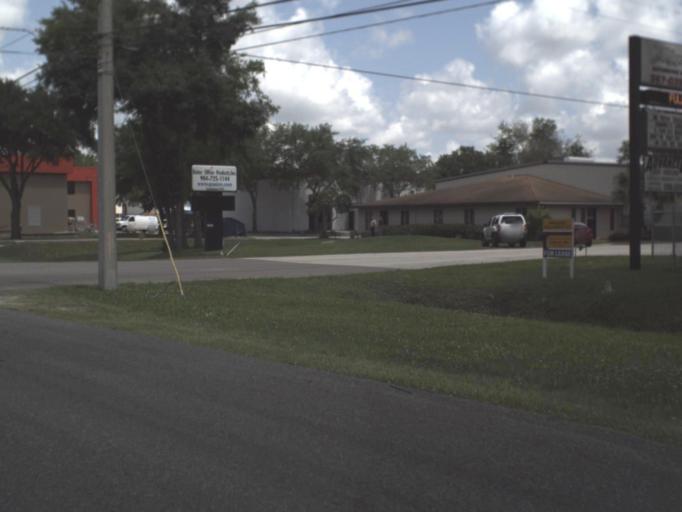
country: US
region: Florida
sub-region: Saint Johns County
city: Fruit Cove
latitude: 30.1558
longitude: -81.5295
